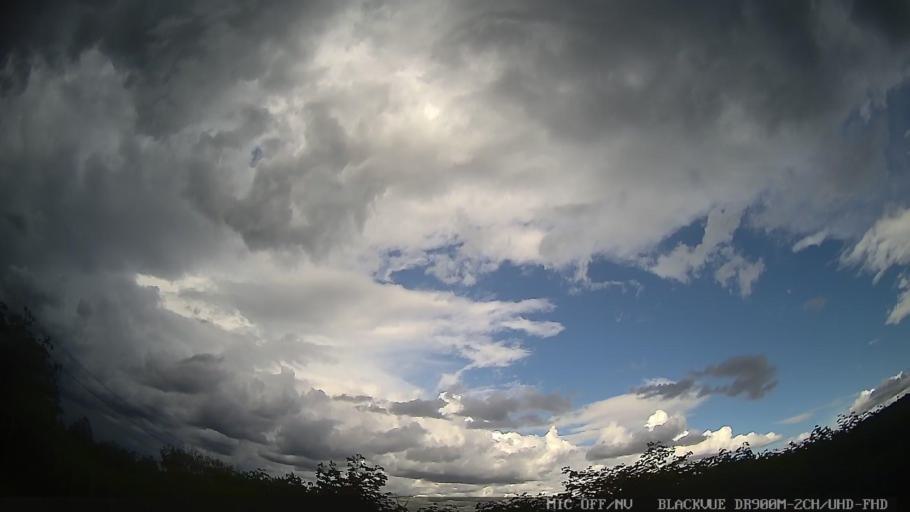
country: BR
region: Sao Paulo
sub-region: Pedreira
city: Pedreira
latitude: -22.7081
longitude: -46.8957
